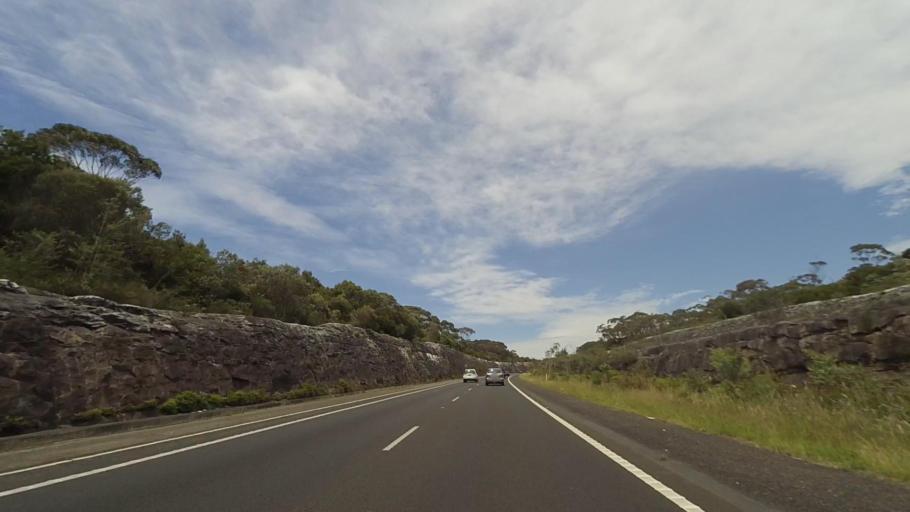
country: AU
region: New South Wales
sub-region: Wollongong
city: Helensburgh
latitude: -34.2388
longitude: 150.9459
